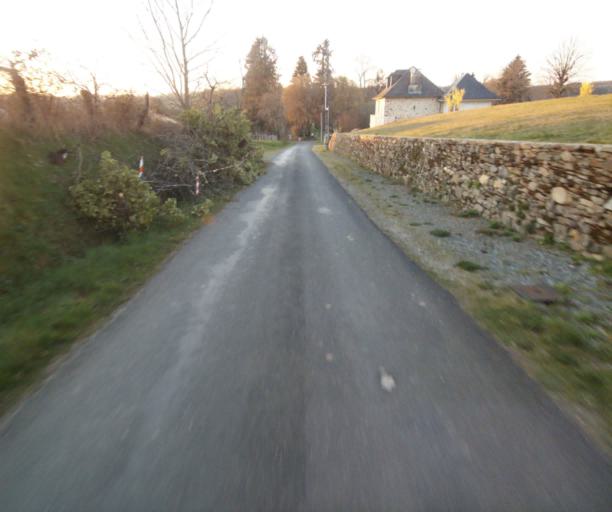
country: FR
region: Limousin
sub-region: Departement de la Correze
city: Saint-Clement
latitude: 45.3649
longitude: 1.6212
